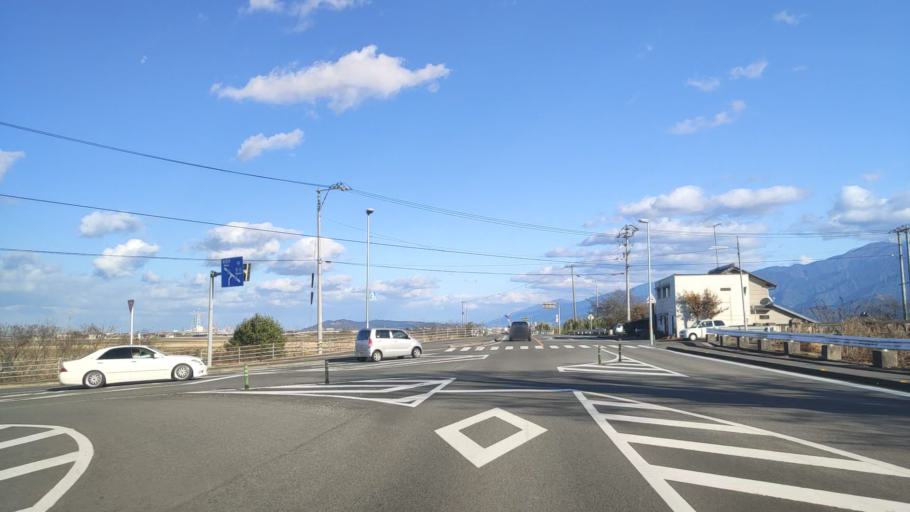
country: JP
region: Ehime
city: Saijo
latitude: 33.9066
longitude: 133.1166
